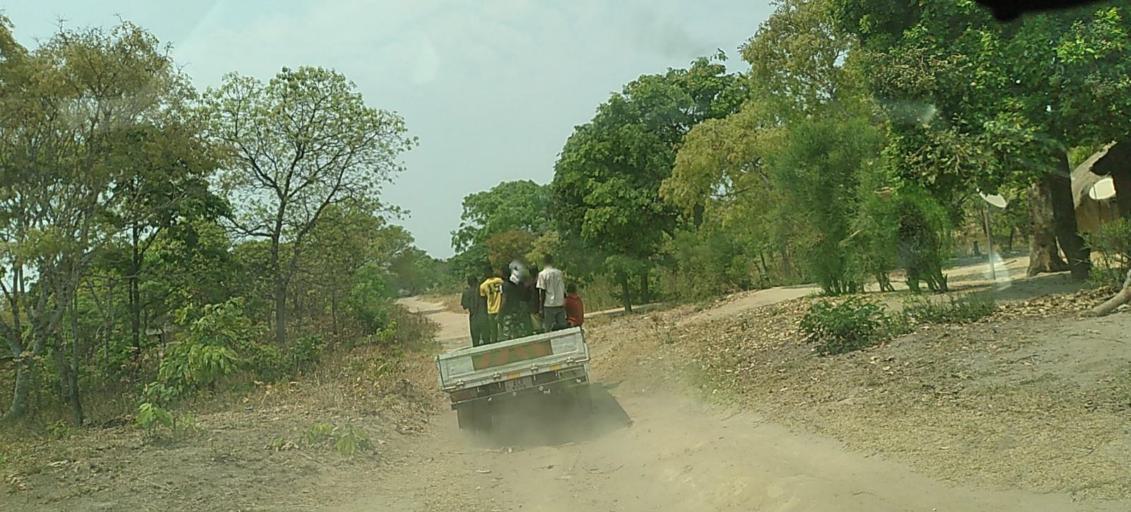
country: ZM
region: North-Western
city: Kabompo
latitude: -13.4840
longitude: 24.4605
